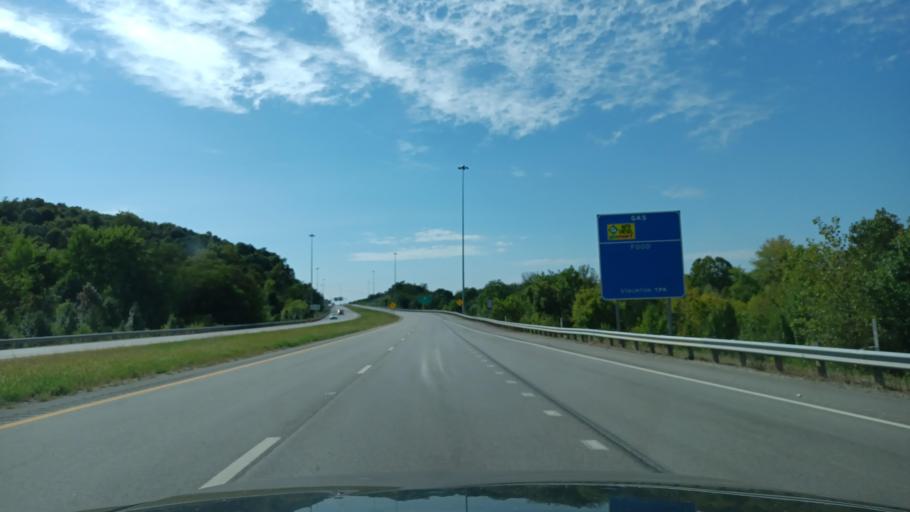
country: US
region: West Virginia
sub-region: Wood County
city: Parkersburg
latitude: 39.2645
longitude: -81.5169
